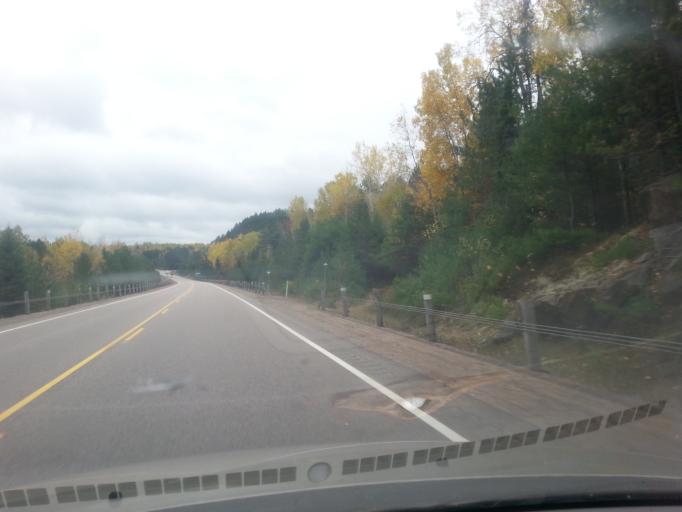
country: CA
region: Ontario
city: Mattawa
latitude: 46.2501
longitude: -78.3169
